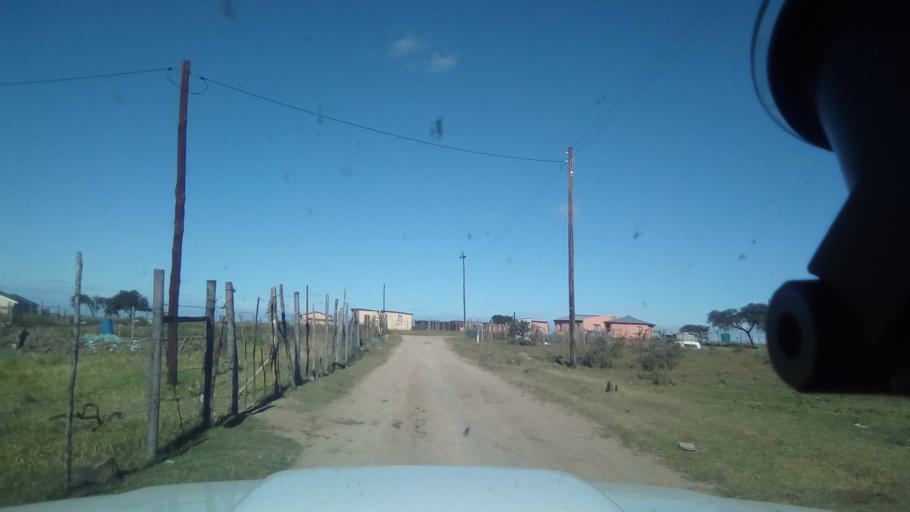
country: ZA
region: Eastern Cape
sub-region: Buffalo City Metropolitan Municipality
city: Bhisho
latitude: -32.7832
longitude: 27.3322
